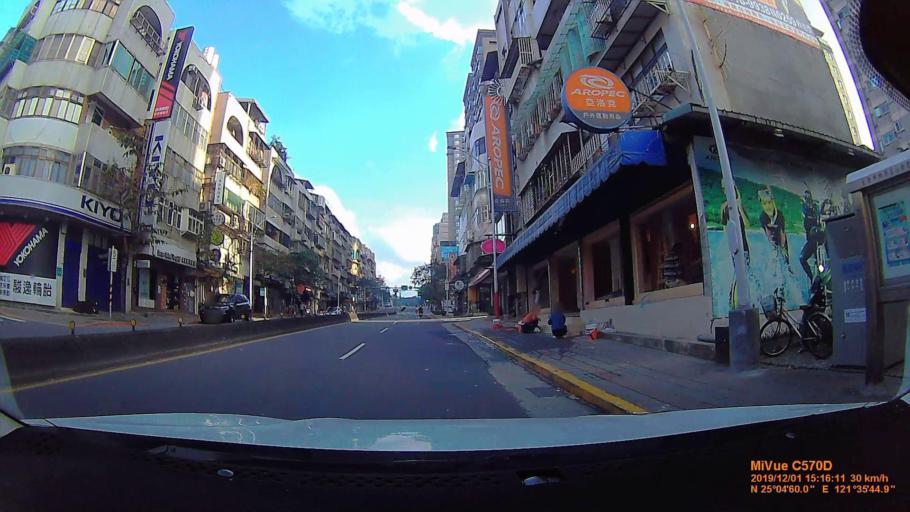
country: TW
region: Taipei
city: Taipei
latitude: 25.0832
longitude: 121.5959
